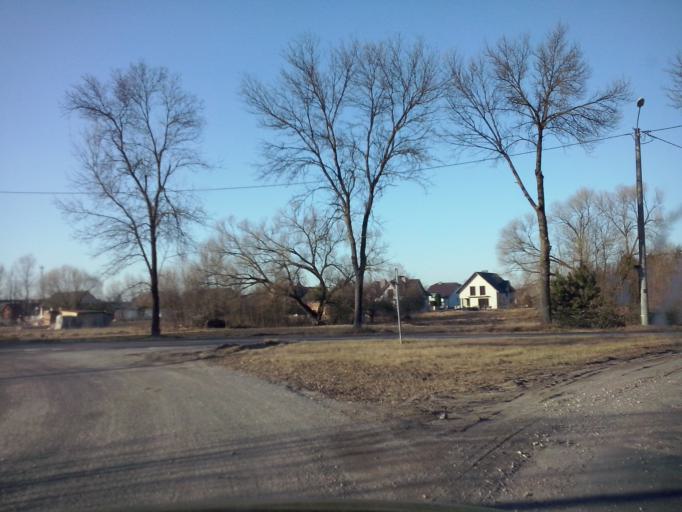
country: PL
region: Subcarpathian Voivodeship
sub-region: Powiat nizanski
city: Harasiuki
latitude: 50.4734
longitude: 22.4720
